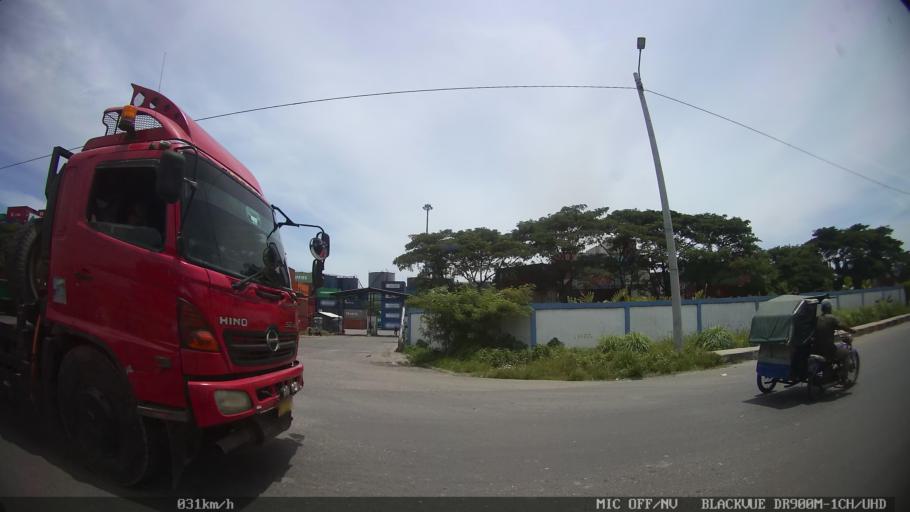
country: ID
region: North Sumatra
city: Belawan
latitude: 3.7799
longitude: 98.6975
